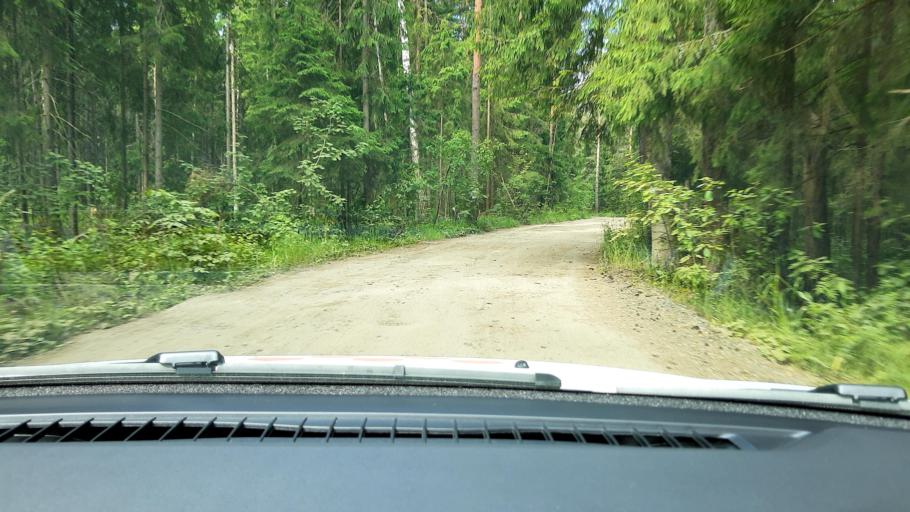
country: RU
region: Nizjnij Novgorod
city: Linda
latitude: 56.6732
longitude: 44.1750
